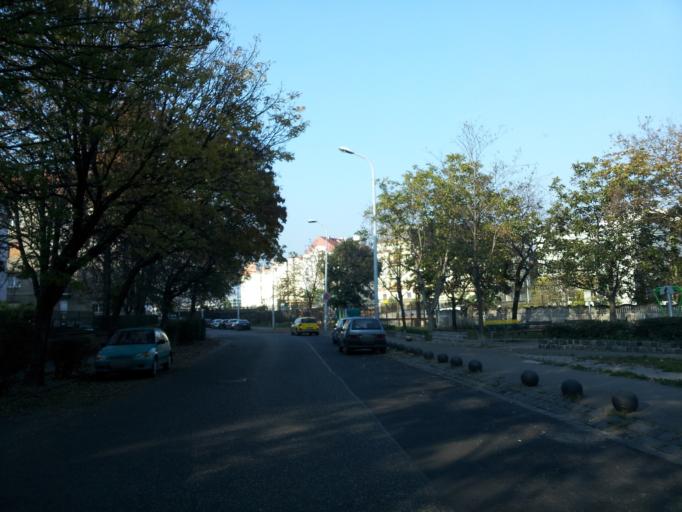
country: HU
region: Budapest
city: Budapest XII. keruelet
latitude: 47.4936
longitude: 19.0268
